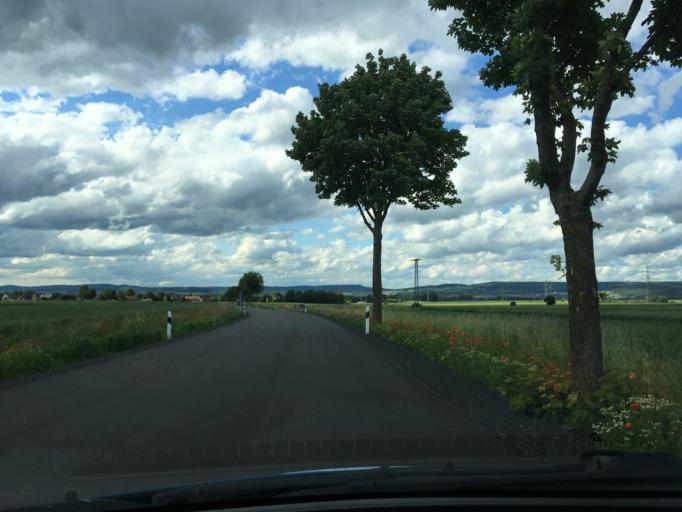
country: DE
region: Lower Saxony
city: Moringen
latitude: 51.7594
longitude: 9.8717
